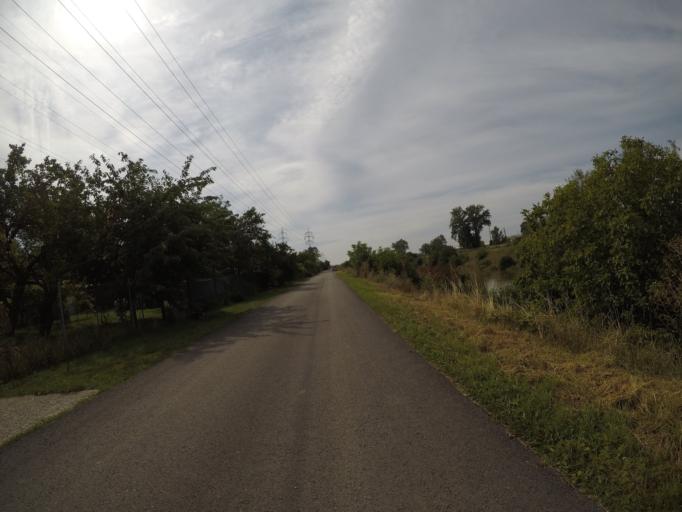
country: SK
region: Trenciansky
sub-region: Okres Nove Mesto nad Vahom
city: Nove Mesto nad Vahom
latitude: 48.7586
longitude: 17.8472
